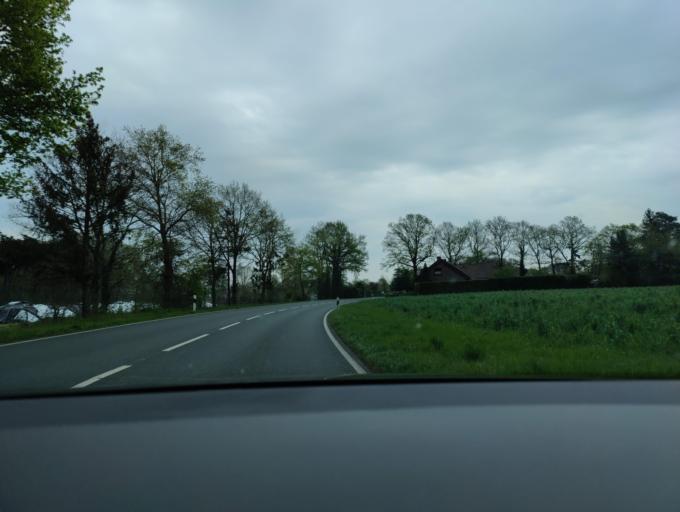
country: DE
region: Lower Saxony
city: Wietmarschen
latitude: 52.5329
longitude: 7.1370
